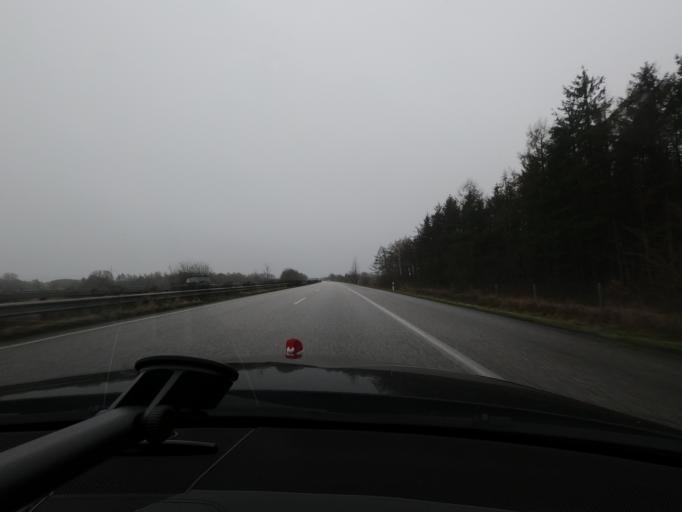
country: DE
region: Schleswig-Holstein
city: Bollingstedt
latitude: 54.6106
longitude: 9.4457
